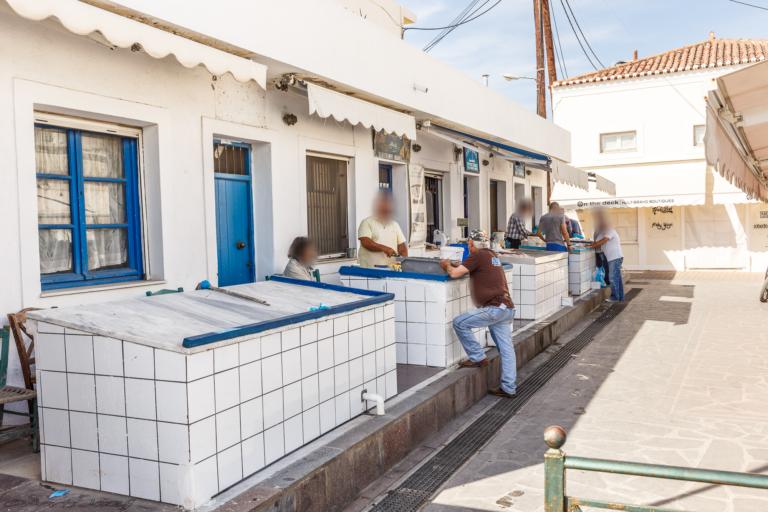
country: GR
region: Attica
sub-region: Nomos Piraios
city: Spetses
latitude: 37.2684
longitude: 23.1555
